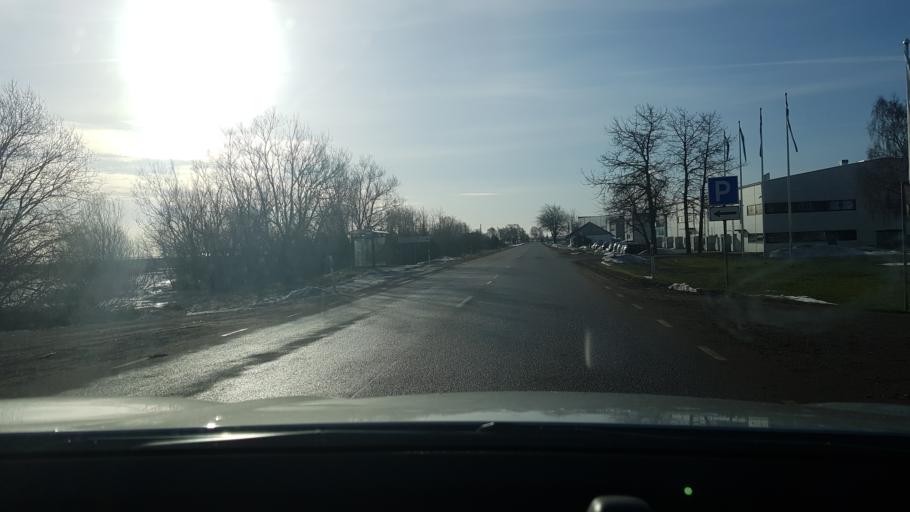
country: EE
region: Saare
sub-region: Kuressaare linn
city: Kuressaare
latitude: 58.2246
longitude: 22.5061
